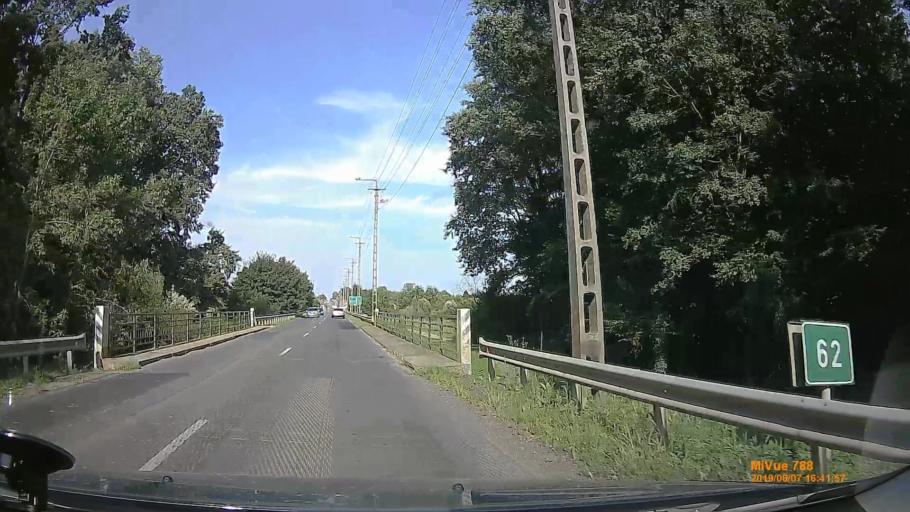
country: HU
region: Zala
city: Lenti
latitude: 46.6278
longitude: 16.5585
